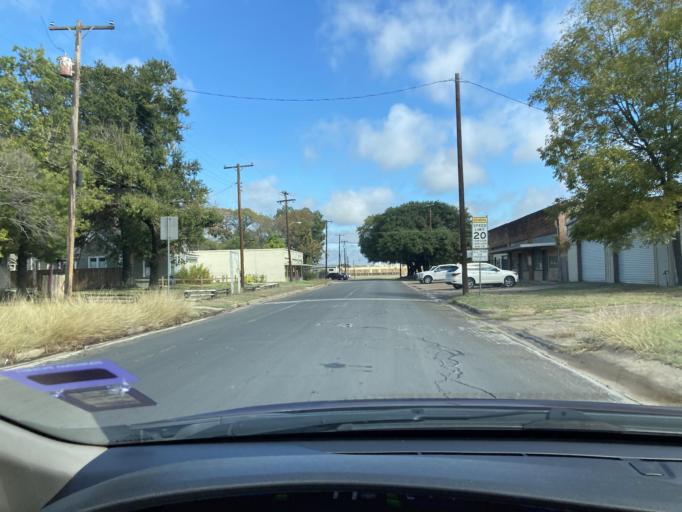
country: US
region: Texas
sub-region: Navarro County
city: Corsicana
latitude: 32.0893
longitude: -96.4738
